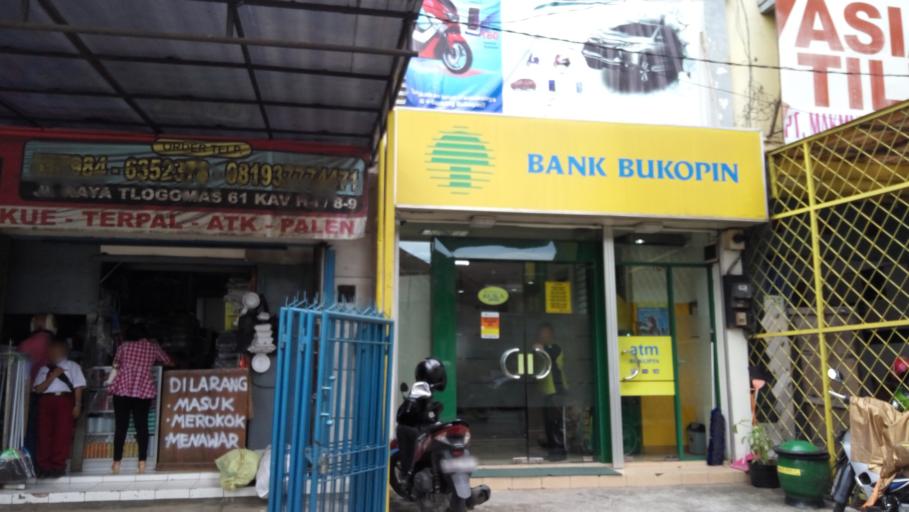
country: ID
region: East Java
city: Malang
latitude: -7.9338
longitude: 112.6038
